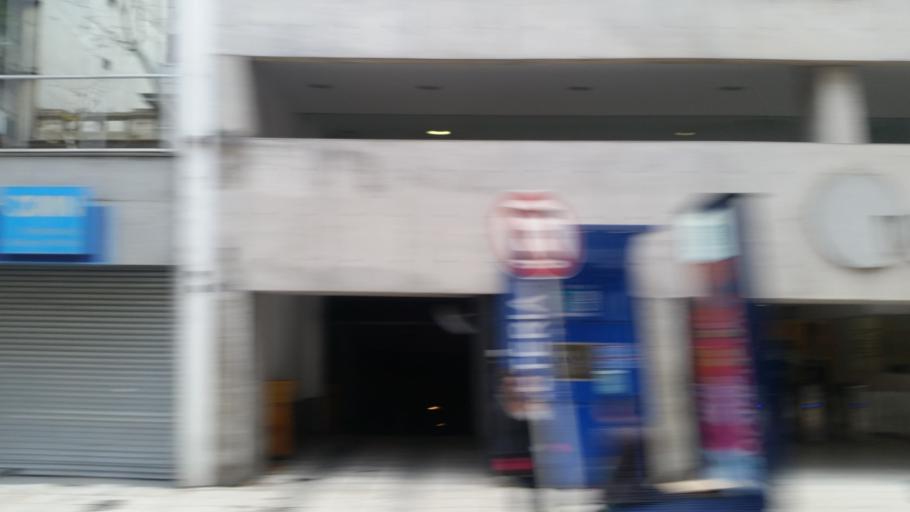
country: AR
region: Buenos Aires F.D.
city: Buenos Aires
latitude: -34.6057
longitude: -58.3958
